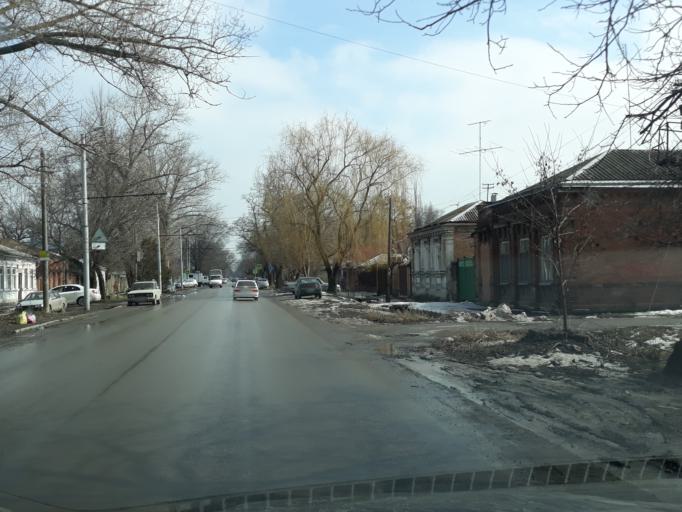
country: RU
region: Rostov
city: Taganrog
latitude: 47.2111
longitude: 38.9125
